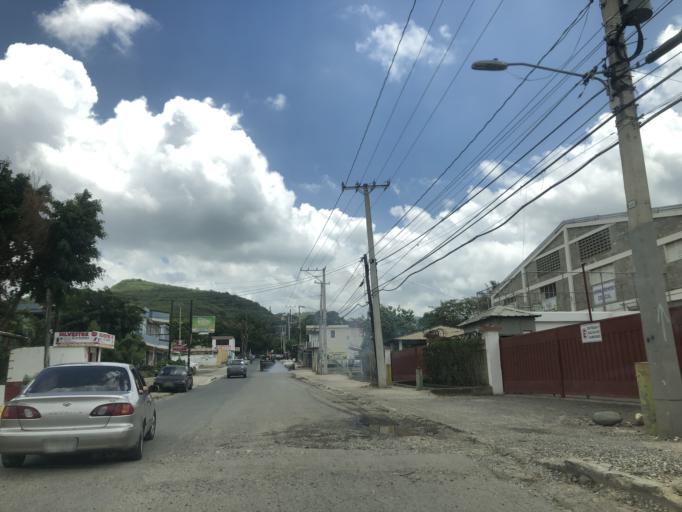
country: DO
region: Santiago
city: Tamboril
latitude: 19.4987
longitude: -70.6521
